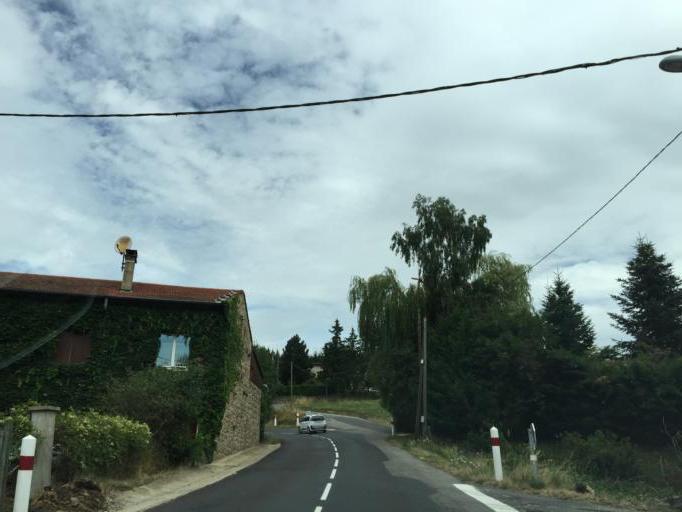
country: FR
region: Rhone-Alpes
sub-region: Departement de la Loire
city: Perigneux
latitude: 45.4055
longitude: 4.1383
